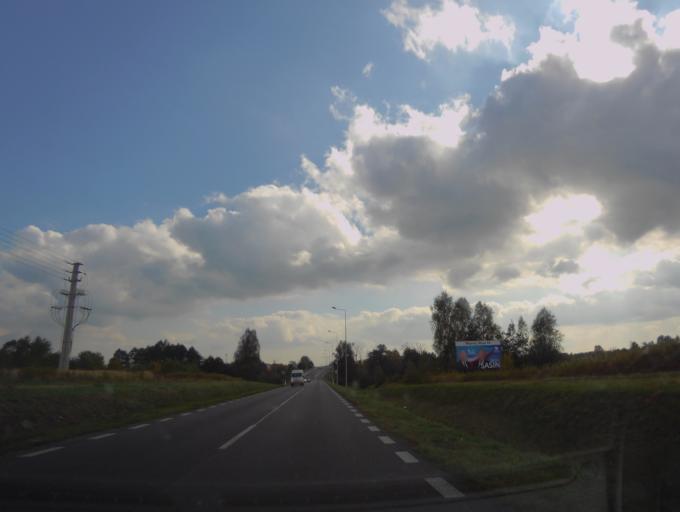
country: PL
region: Lublin Voivodeship
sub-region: Powiat bilgorajski
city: Bilgoraj
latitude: 50.5533
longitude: 22.7008
